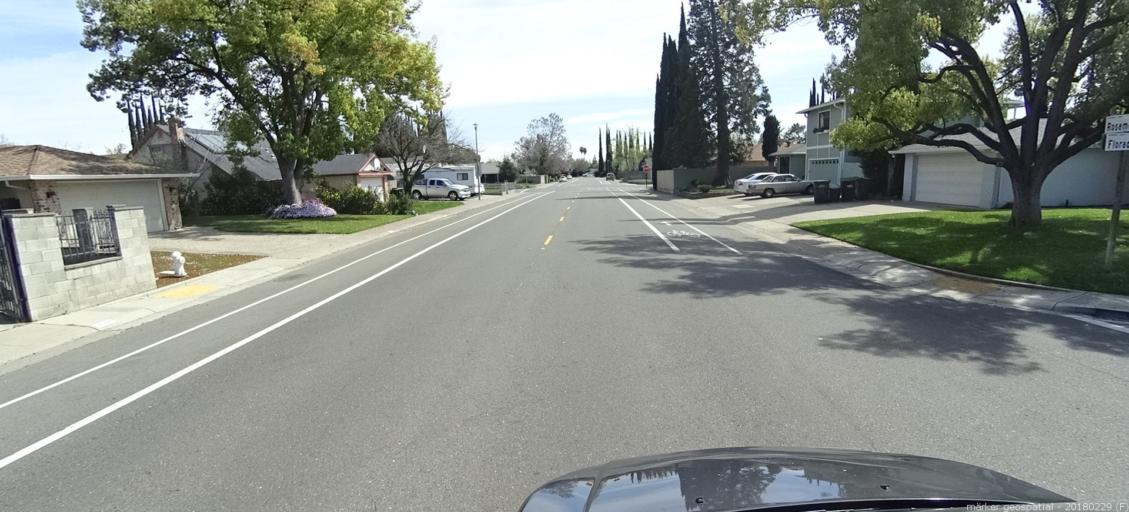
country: US
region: California
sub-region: Sacramento County
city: Rosemont
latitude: 38.5550
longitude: -121.3556
